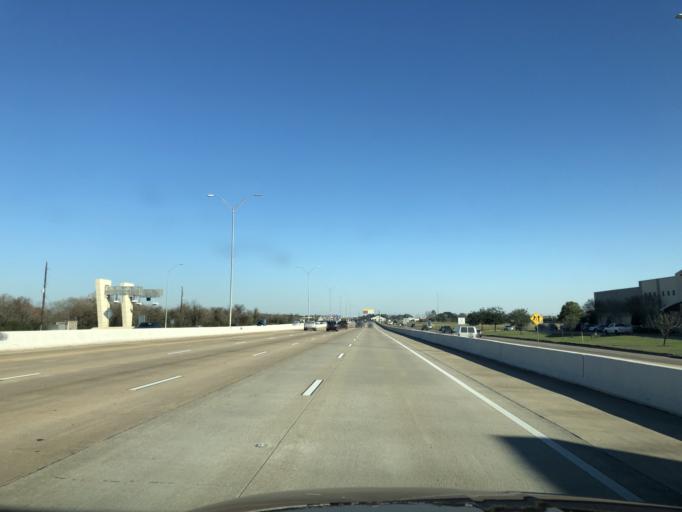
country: US
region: Texas
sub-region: Fort Bend County
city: Fresno
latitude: 29.5964
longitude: -95.4402
